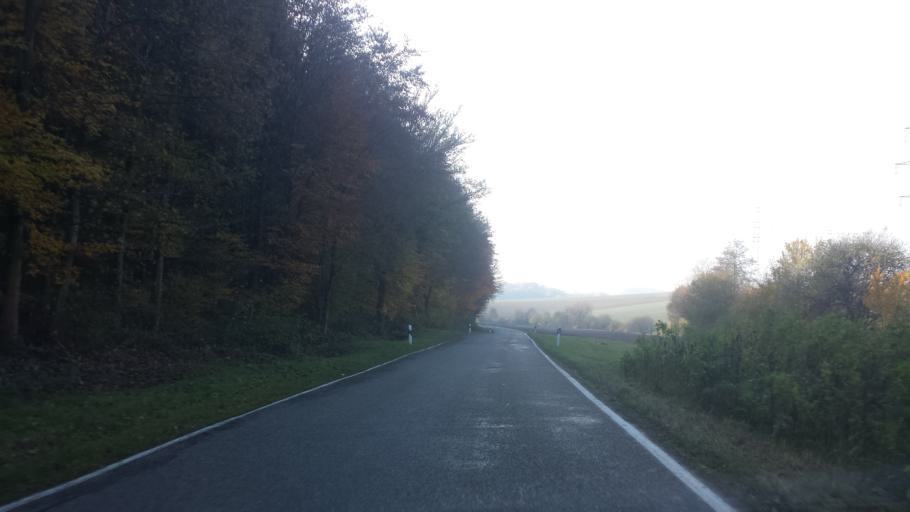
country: DE
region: Baden-Wuerttemberg
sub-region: Karlsruhe Region
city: Aglasterhausen
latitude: 49.3169
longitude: 9.0053
